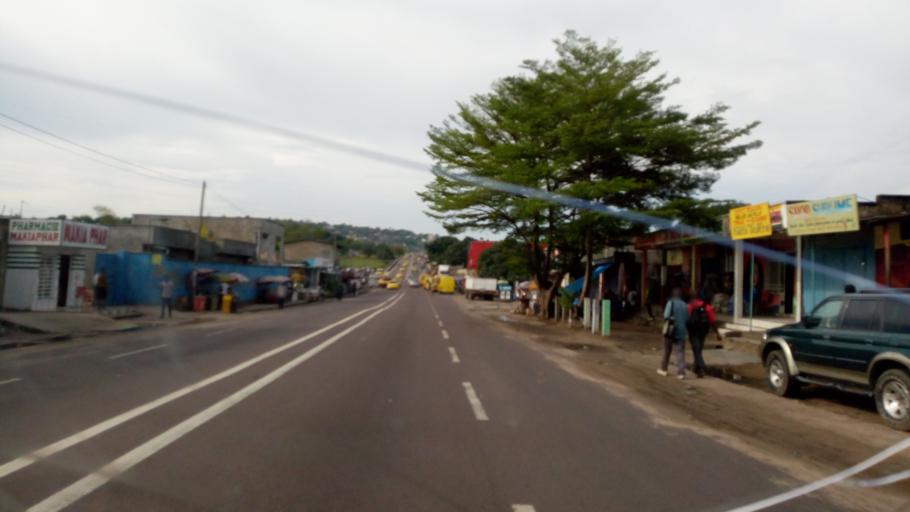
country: CD
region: Kinshasa
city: Kinshasa
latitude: -4.4349
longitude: 15.2581
